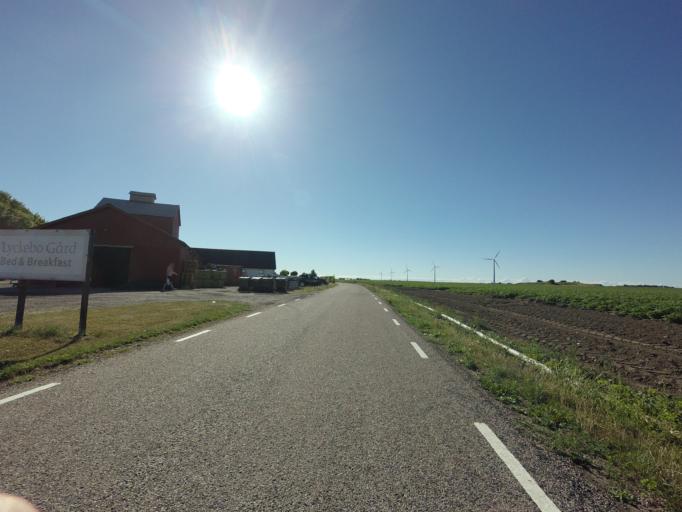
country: SE
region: Skane
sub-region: Trelleborgs Kommun
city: Skare
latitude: 55.3952
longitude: 13.0292
